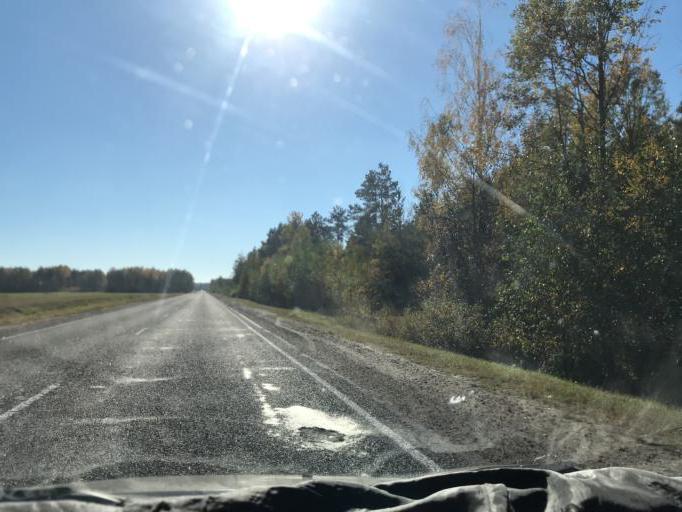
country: BY
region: Gomel
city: Sasnovy Bor
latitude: 52.5595
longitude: 29.3590
